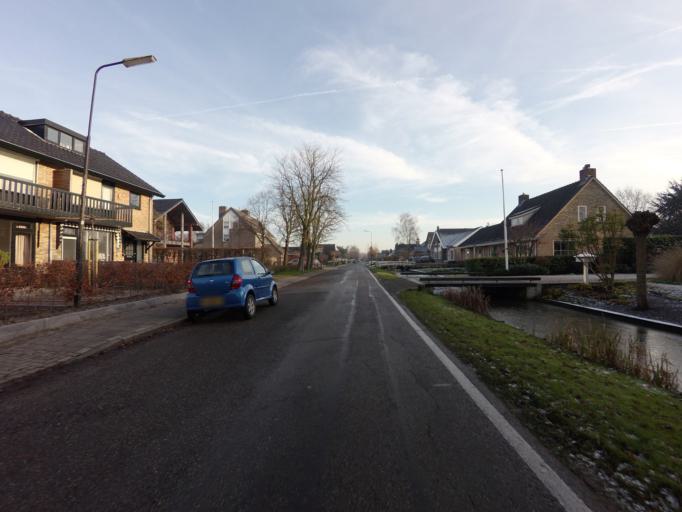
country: NL
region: Utrecht
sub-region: Gemeente De Ronde Venen
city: Mijdrecht
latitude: 52.1960
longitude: 4.8875
